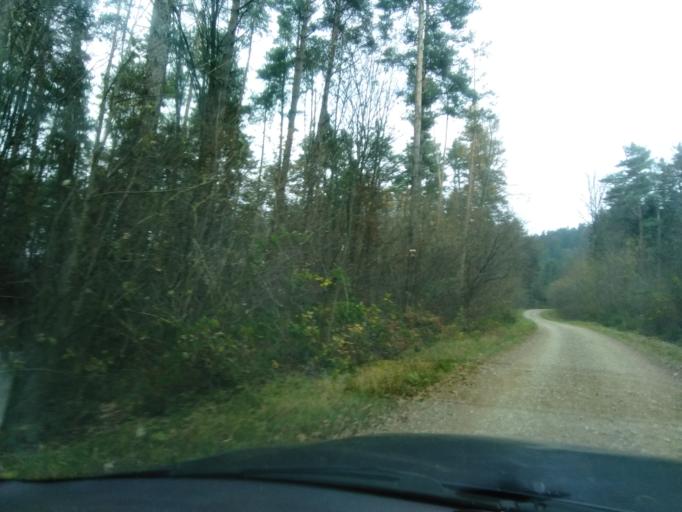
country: PL
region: Subcarpathian Voivodeship
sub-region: Powiat strzyzowski
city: Wysoka Strzyzowska
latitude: 49.7894
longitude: 21.7671
